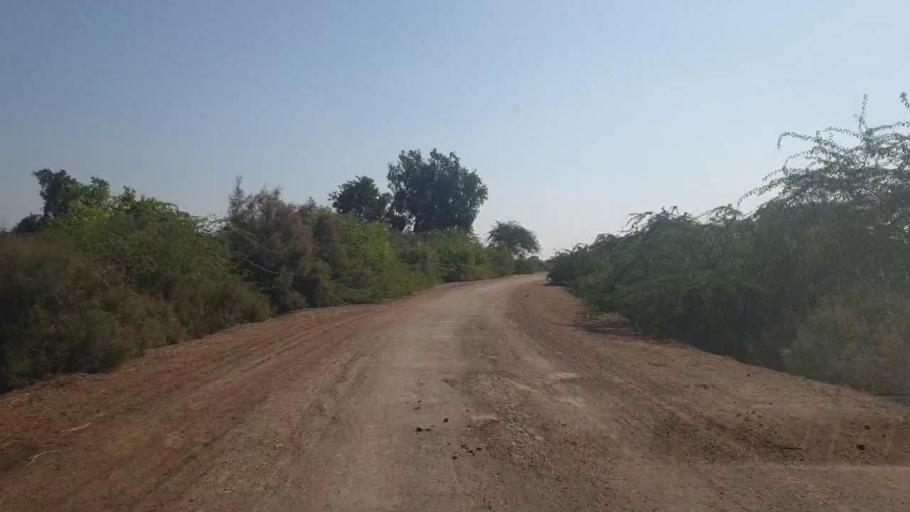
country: PK
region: Sindh
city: Badin
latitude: 24.5707
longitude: 68.8455
